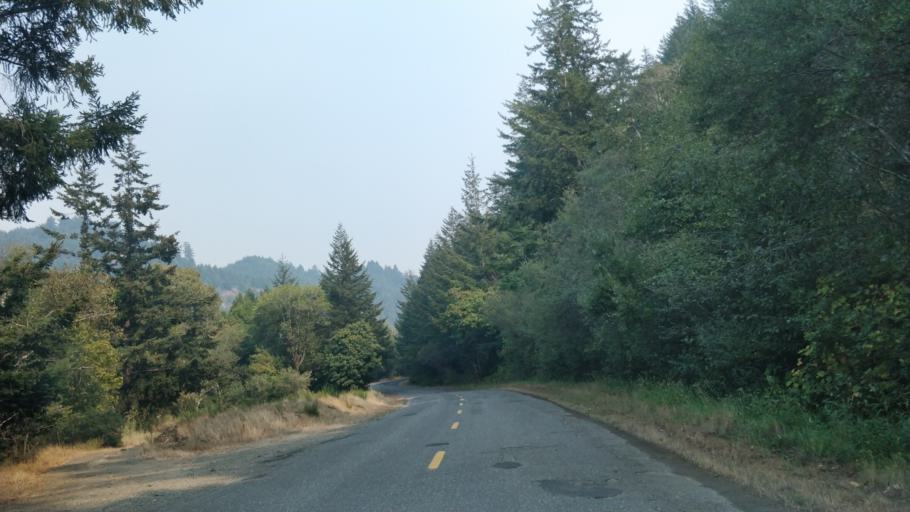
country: US
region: California
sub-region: Humboldt County
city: Rio Dell
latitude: 40.3107
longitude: -124.2672
